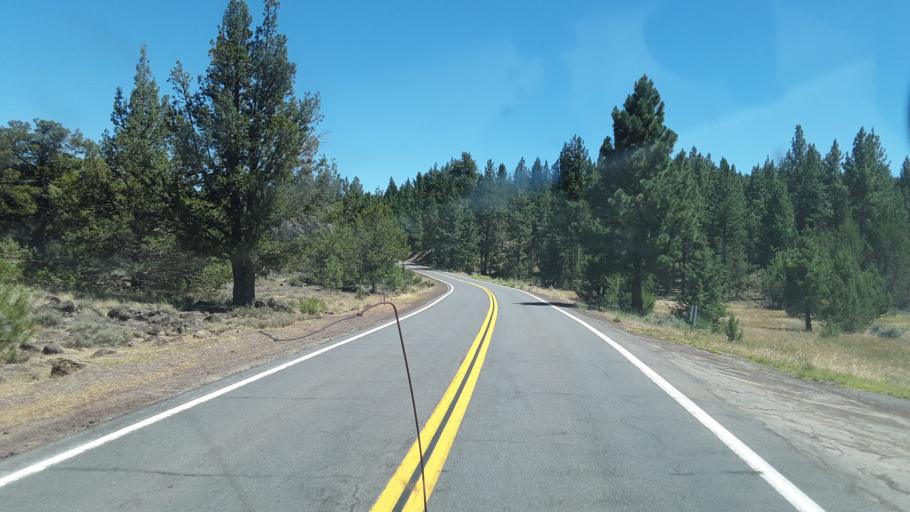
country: US
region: California
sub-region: Lassen County
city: Johnstonville
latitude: 40.4918
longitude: -120.5567
